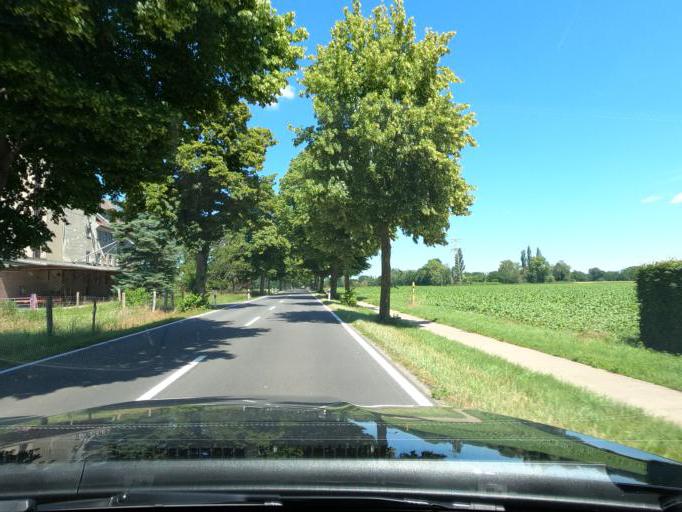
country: DE
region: Lower Saxony
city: Lehrte
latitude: 52.4089
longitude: 9.9749
